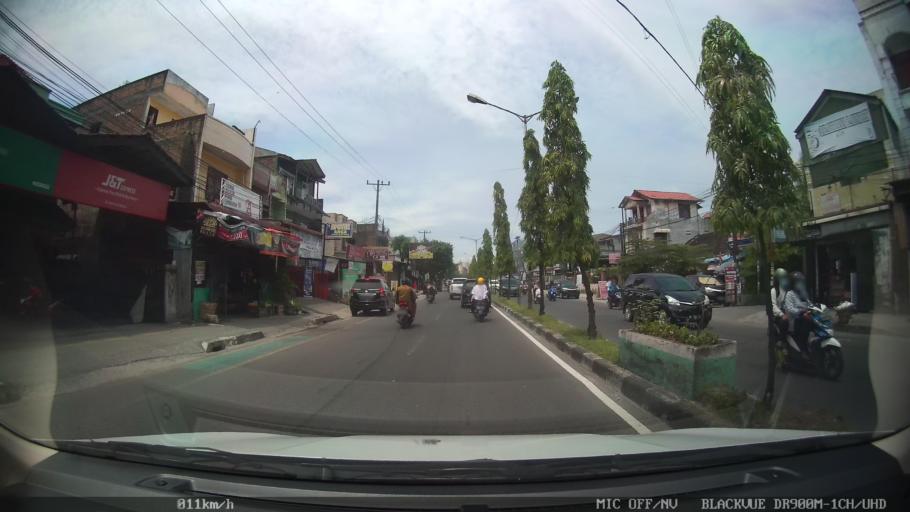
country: ID
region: North Sumatra
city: Sunggal
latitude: 3.5445
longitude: 98.6251
